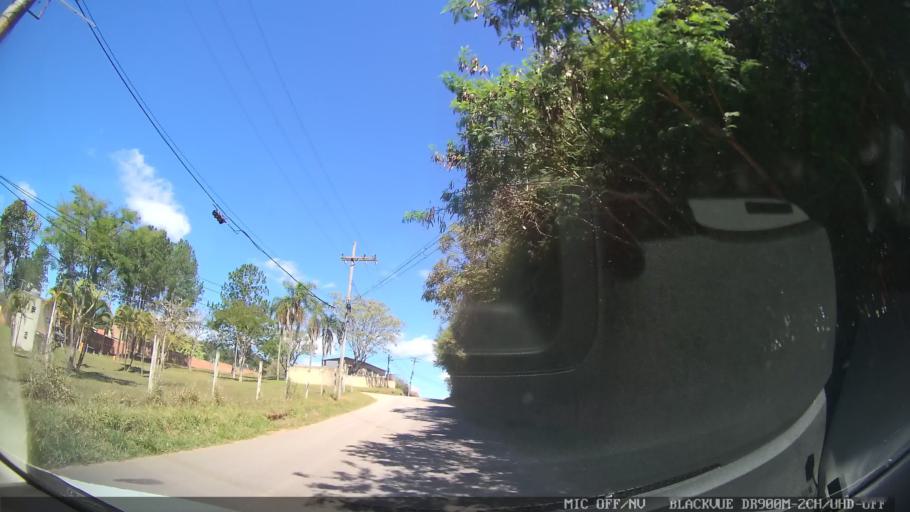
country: BR
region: Sao Paulo
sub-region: Campo Limpo Paulista
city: Campo Limpo Paulista
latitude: -23.1769
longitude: -46.7414
